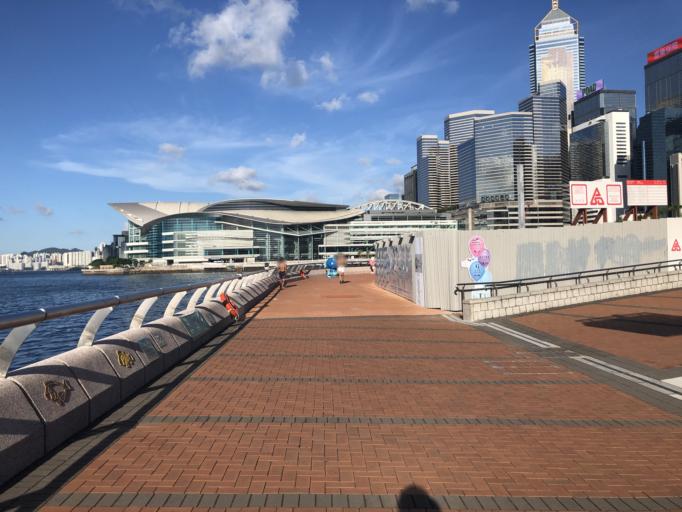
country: HK
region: Wanchai
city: Wan Chai
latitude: 22.2832
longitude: 114.1672
